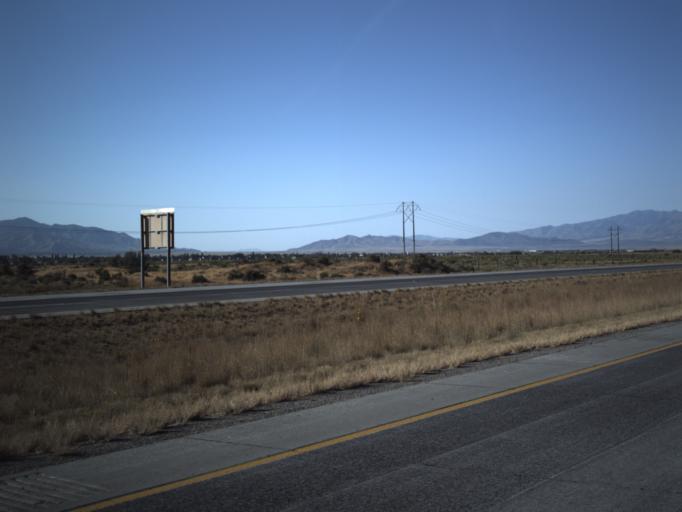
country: US
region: Utah
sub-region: Tooele County
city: Stansbury park
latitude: 40.6729
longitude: -112.2920
